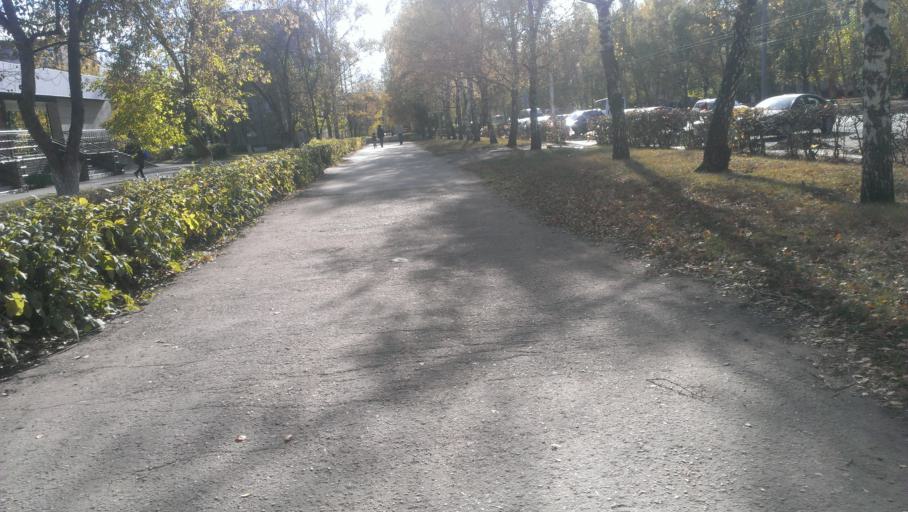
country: RU
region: Altai Krai
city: Novosilikatnyy
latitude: 53.3531
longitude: 83.6843
